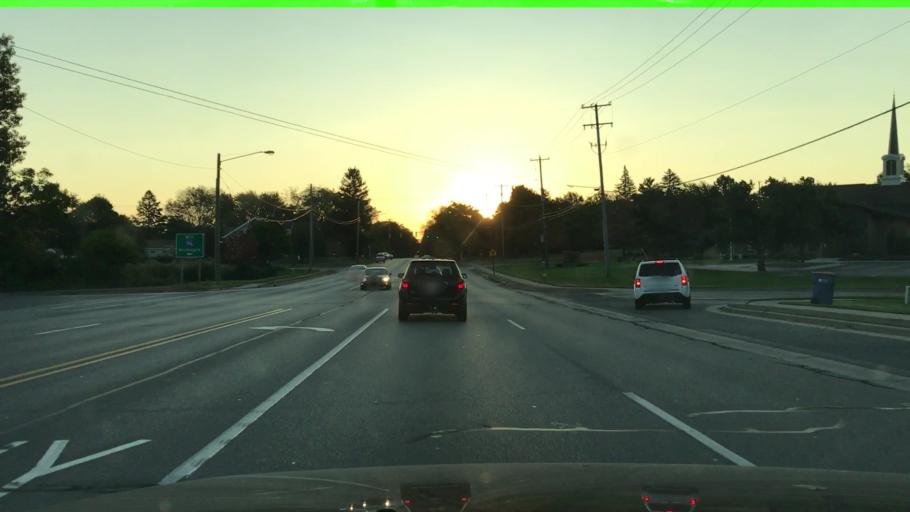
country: US
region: Michigan
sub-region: Kent County
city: East Grand Rapids
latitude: 42.9843
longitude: -85.6032
